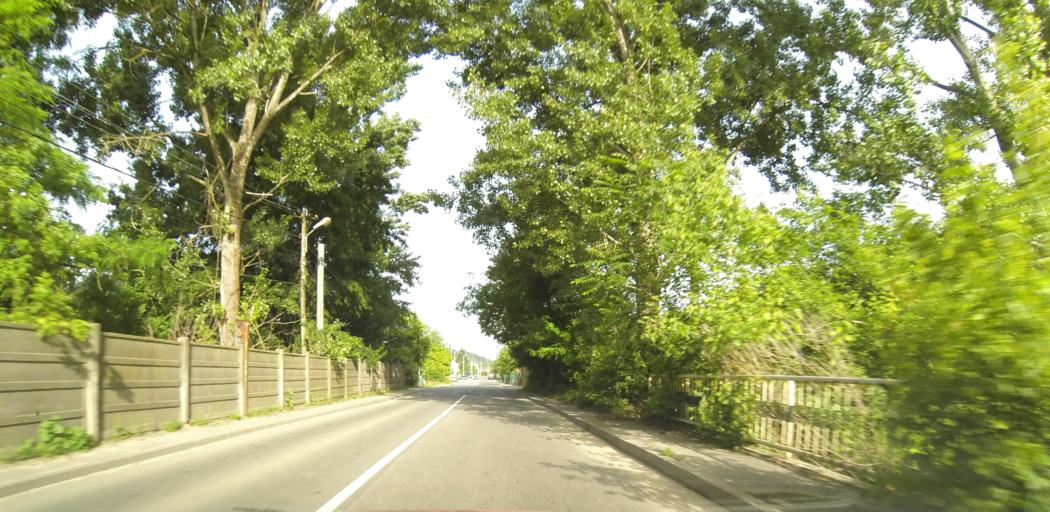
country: RO
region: Valcea
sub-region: Comuna Bujoreni
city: Bujoreni
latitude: 45.1096
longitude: 24.3329
